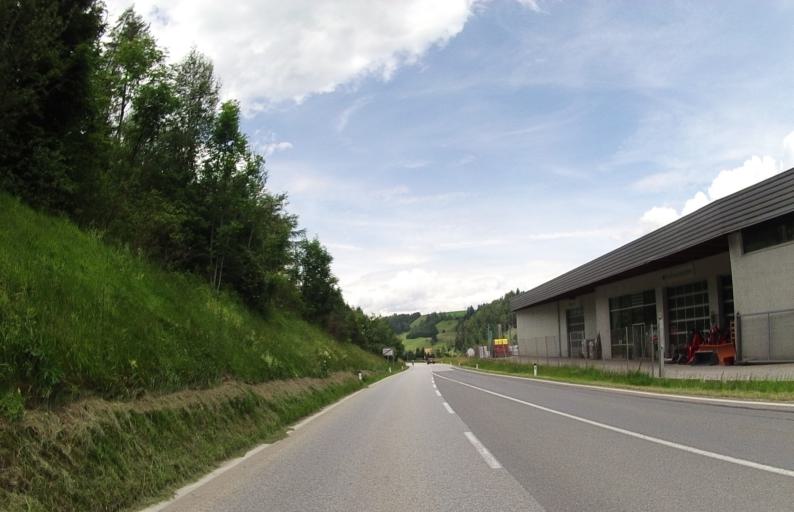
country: AT
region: Tyrol
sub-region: Politischer Bezirk Innsbruck Land
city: Steinach am Brenner
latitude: 47.0998
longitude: 11.4634
